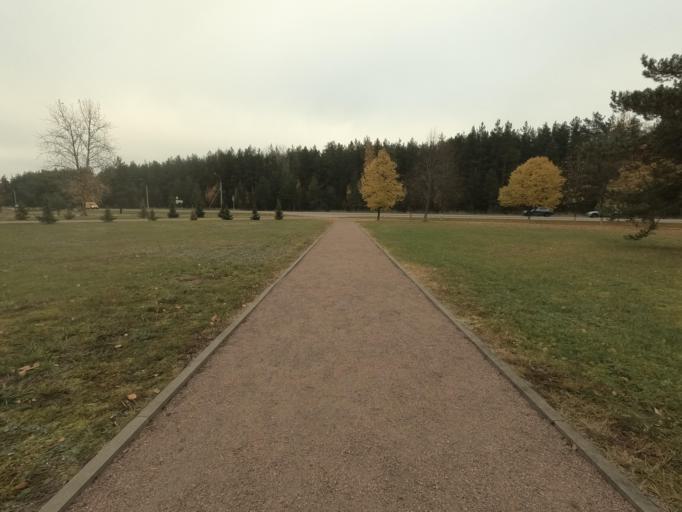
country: RU
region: Leningrad
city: Kirovsk
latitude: 59.8481
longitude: 30.9569
